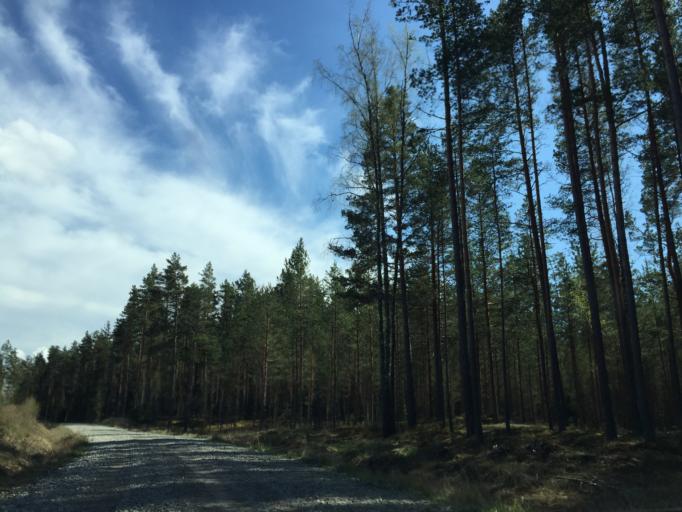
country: LV
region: Strenci
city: Strenci
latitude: 57.5948
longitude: 25.6921
